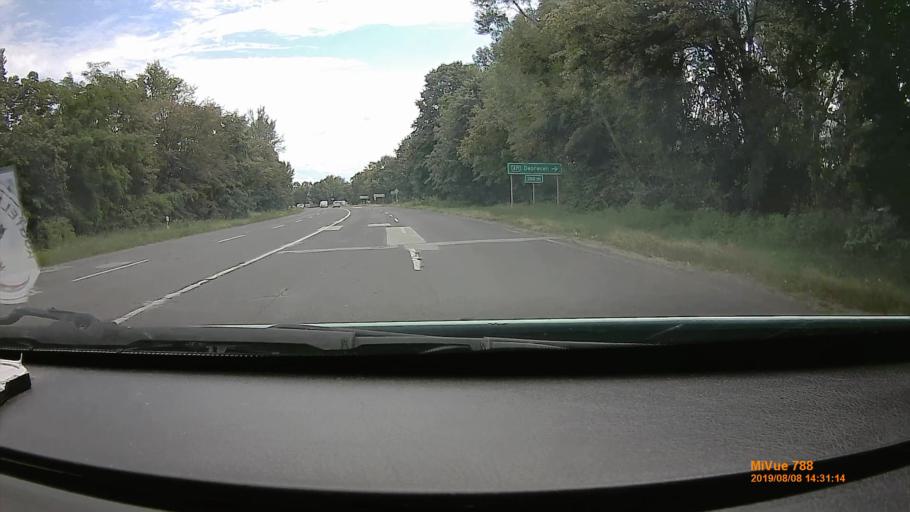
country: HU
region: Szabolcs-Szatmar-Bereg
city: Mateszalka
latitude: 47.9432
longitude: 22.3262
